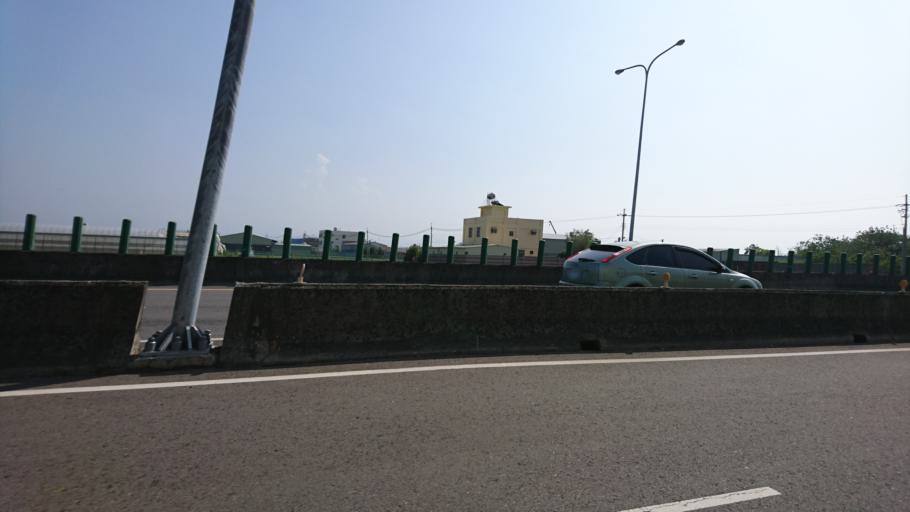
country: TW
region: Taiwan
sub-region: Miaoli
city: Miaoli
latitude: 24.6844
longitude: 120.8504
